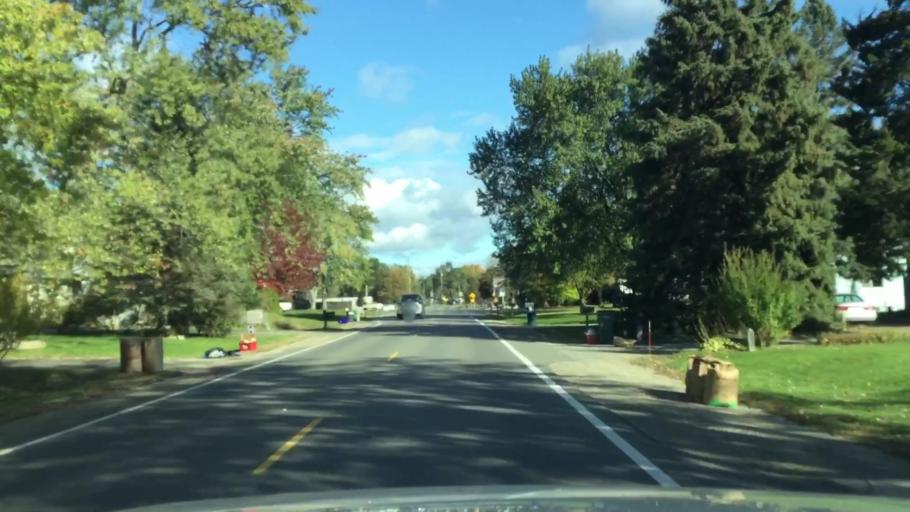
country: US
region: Michigan
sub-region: Oakland County
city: Waterford
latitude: 42.6793
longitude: -83.3815
